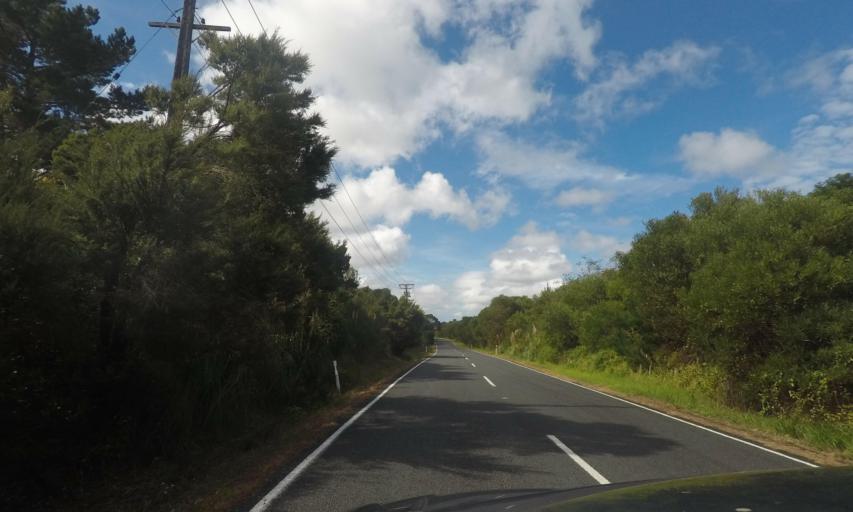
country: NZ
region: Auckland
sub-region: Auckland
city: Rosebank
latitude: -36.7873
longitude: 174.6408
